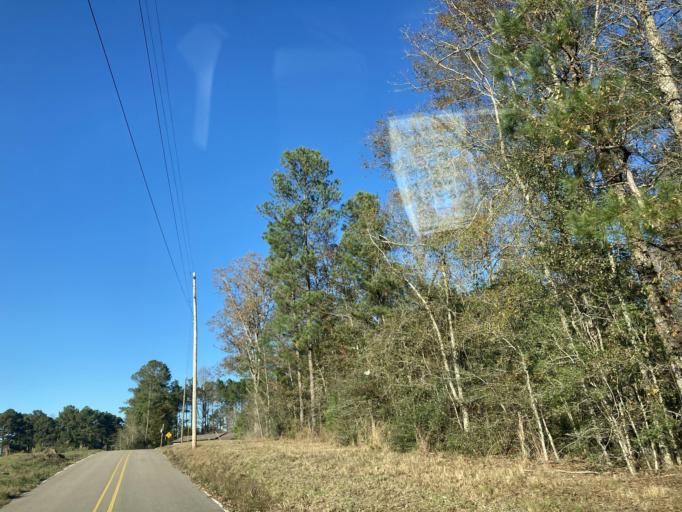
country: US
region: Mississippi
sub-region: Lamar County
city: Sumrall
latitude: 31.4016
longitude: -89.5822
